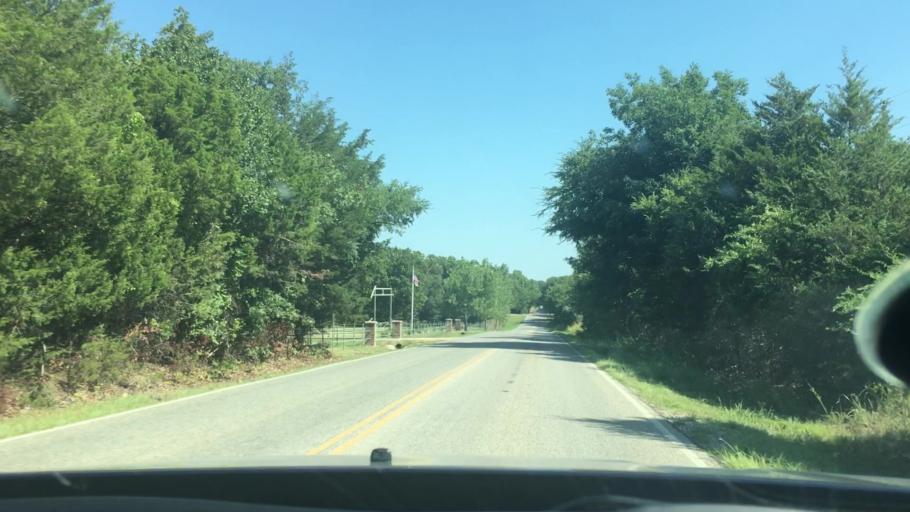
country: US
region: Oklahoma
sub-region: Johnston County
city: Tishomingo
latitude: 34.2603
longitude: -96.6186
